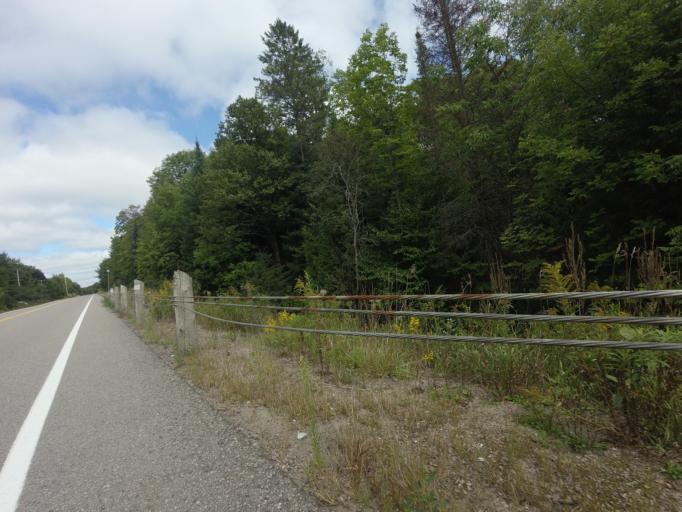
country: CA
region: Ontario
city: Bancroft
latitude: 44.9411
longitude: -78.3006
